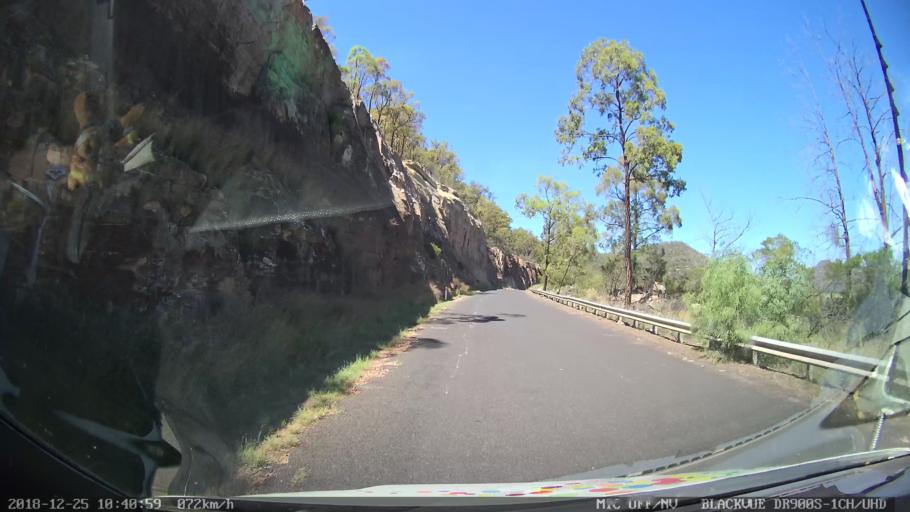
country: AU
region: New South Wales
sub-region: Upper Hunter Shire
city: Merriwa
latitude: -32.4132
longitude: 150.3393
